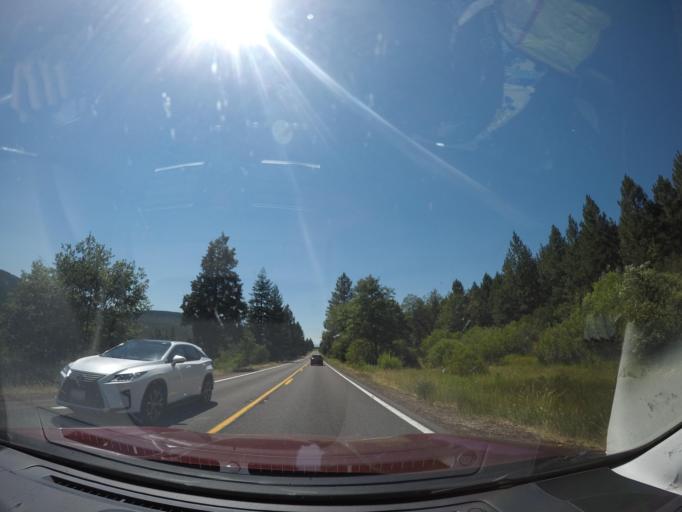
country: US
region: California
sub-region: Shasta County
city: Burney
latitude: 40.8627
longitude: -121.7993
